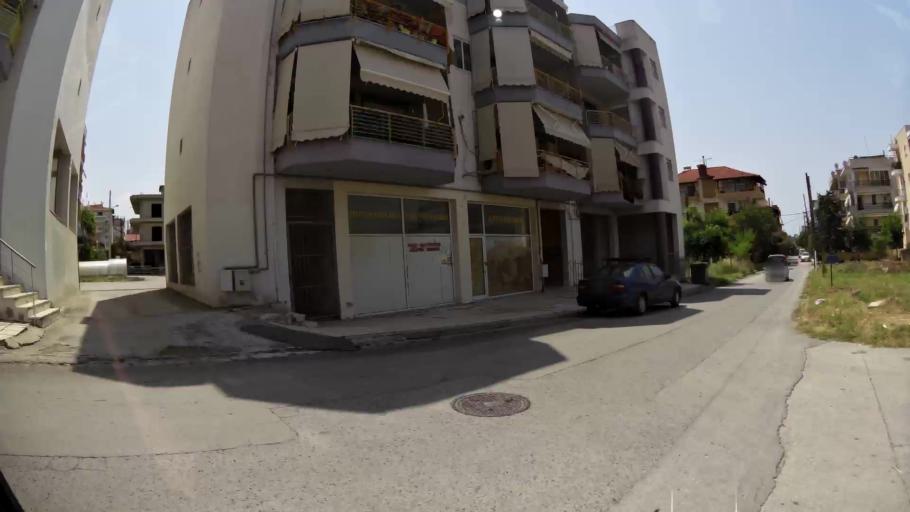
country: GR
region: Central Macedonia
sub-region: Nomos Thessalonikis
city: Evosmos
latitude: 40.6763
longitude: 22.8963
